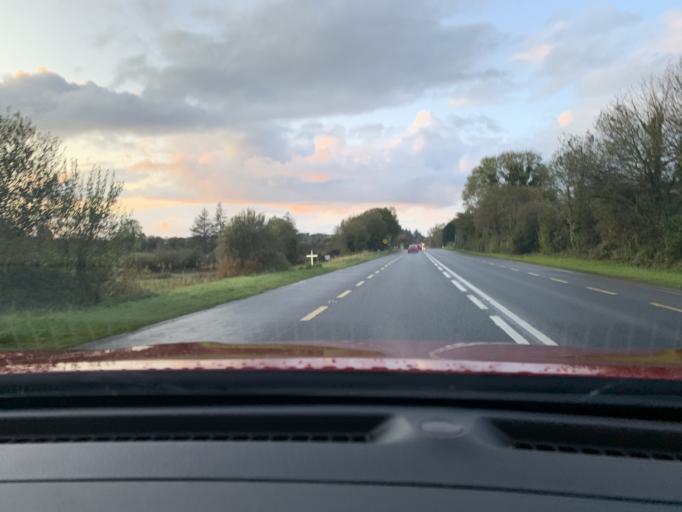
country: IE
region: Connaught
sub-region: Sligo
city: Ballymote
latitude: 54.0819
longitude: -8.3798
